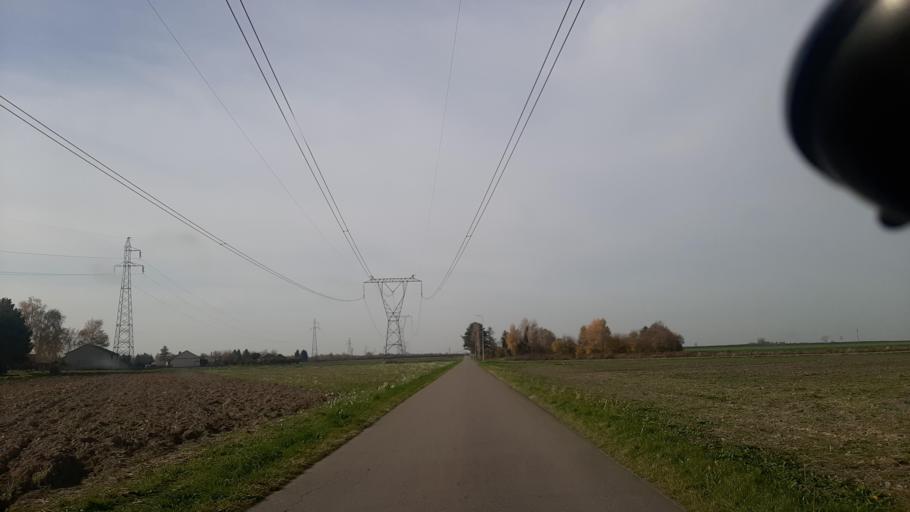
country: PL
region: Lublin Voivodeship
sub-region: Powiat lubelski
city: Lublin
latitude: 51.3329
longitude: 22.5404
